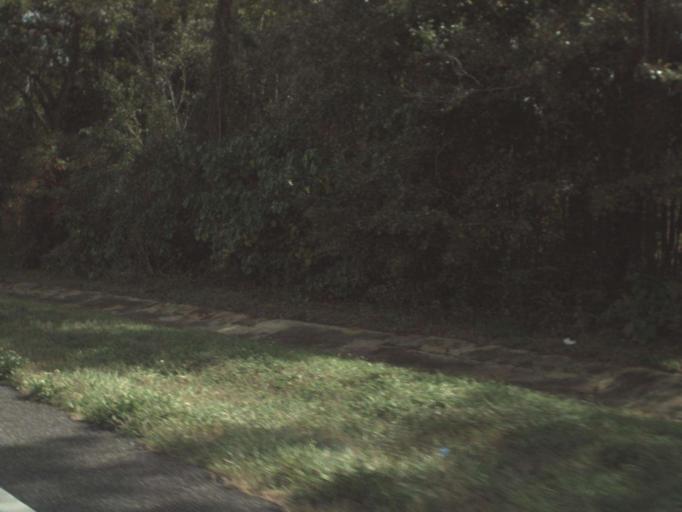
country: US
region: Florida
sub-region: Jefferson County
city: Monticello
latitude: 30.3984
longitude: -83.8779
